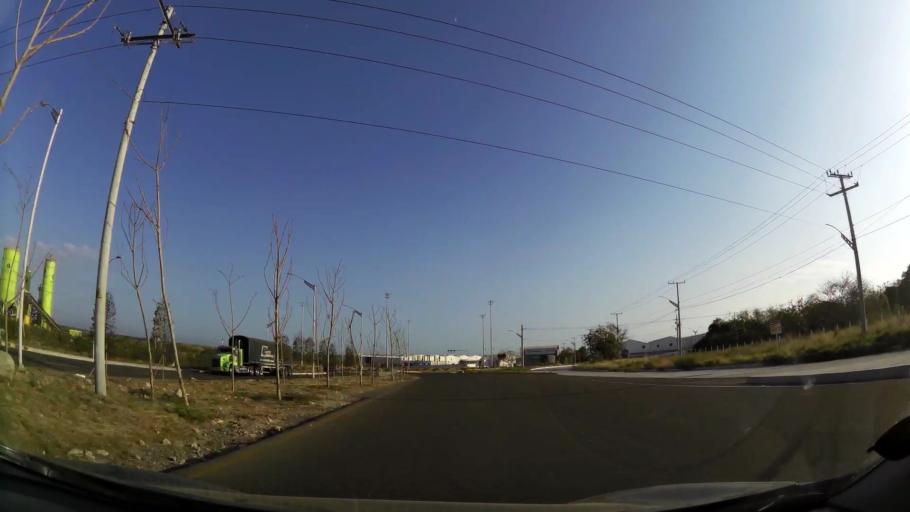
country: CO
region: Atlantico
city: Barranquilla
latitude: 11.0319
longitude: -74.8318
